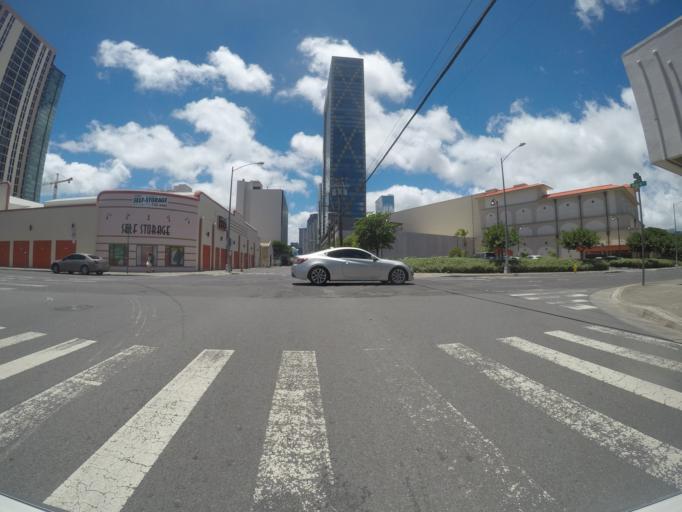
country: US
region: Hawaii
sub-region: Honolulu County
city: Honolulu
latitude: 21.2954
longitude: -157.8504
